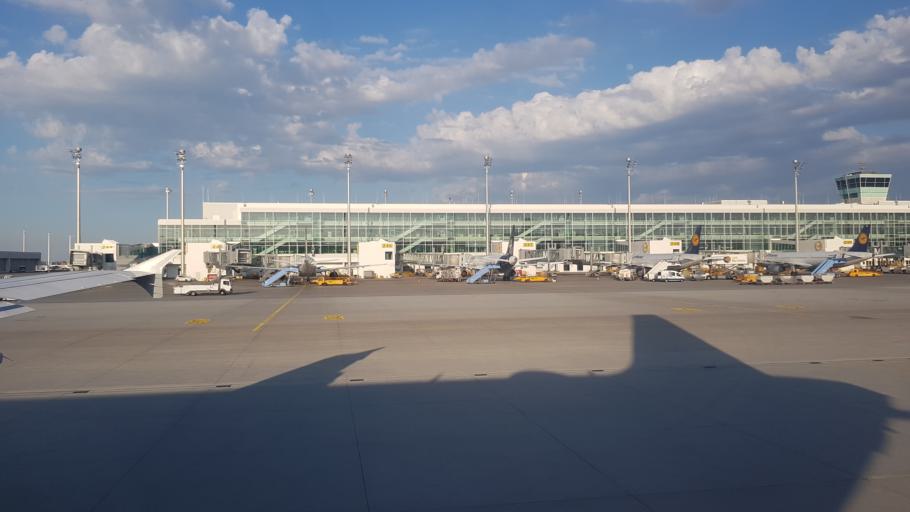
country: DE
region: Bavaria
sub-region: Upper Bavaria
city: Hallbergmoos
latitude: 48.3566
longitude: 11.7948
